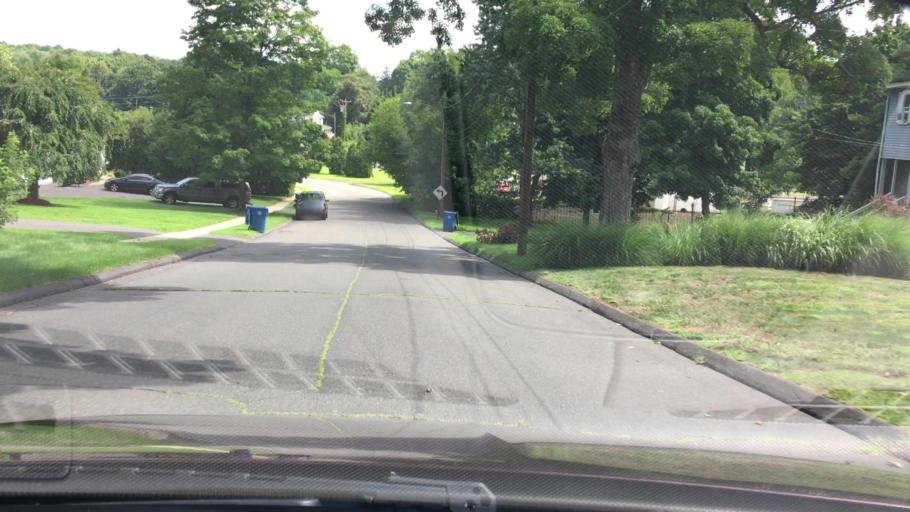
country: US
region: Connecticut
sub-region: Hartford County
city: Kensington
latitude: 41.6142
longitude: -72.7464
